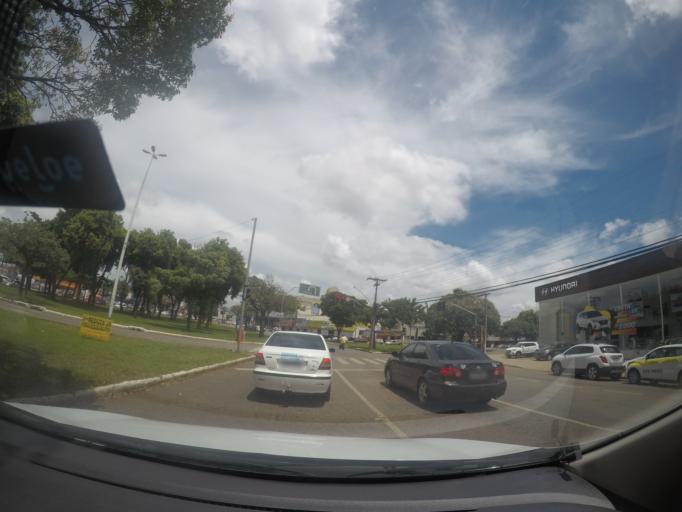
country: BR
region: Goias
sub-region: Goiania
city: Goiania
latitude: -16.6813
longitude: -49.3101
